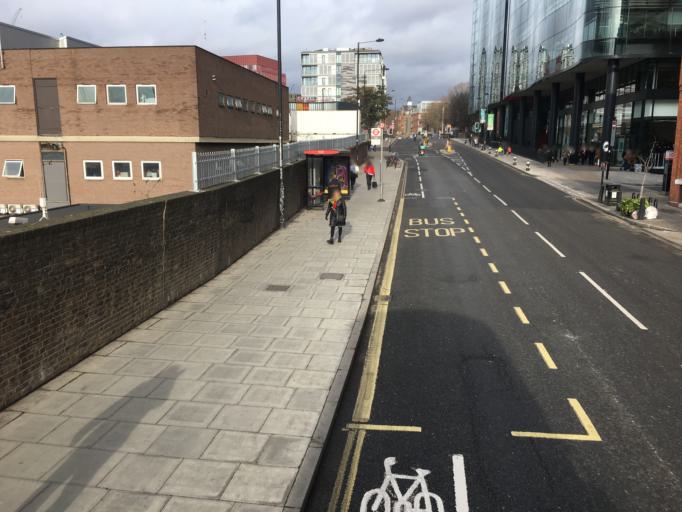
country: GB
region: England
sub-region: Greater London
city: Barnsbury
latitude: 51.5342
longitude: -0.1223
